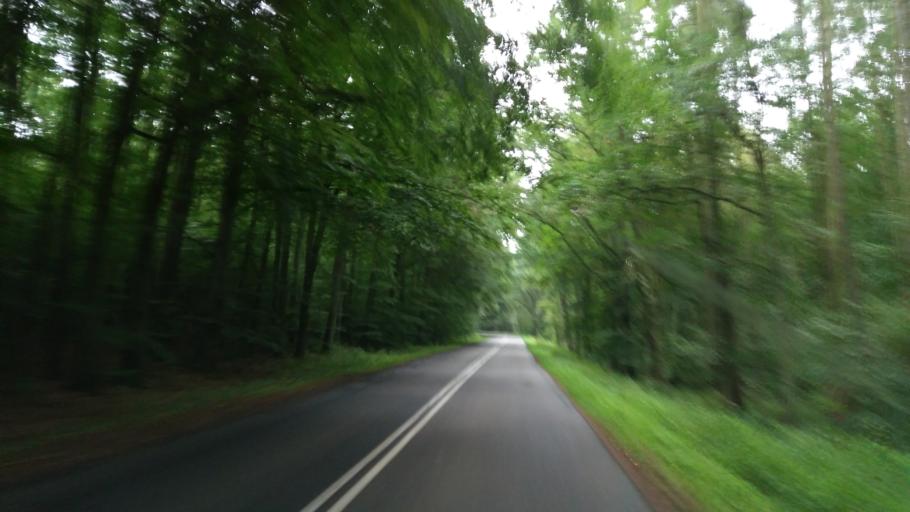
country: PL
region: West Pomeranian Voivodeship
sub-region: Powiat choszczenski
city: Pelczyce
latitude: 53.0767
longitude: 15.2878
